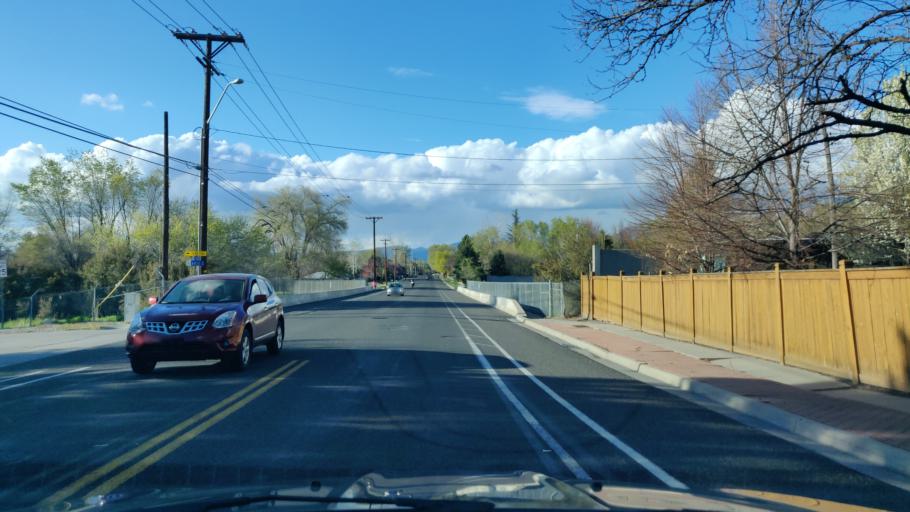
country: US
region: Utah
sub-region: Salt Lake County
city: Cottonwood Heights
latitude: 40.6337
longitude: -111.8247
